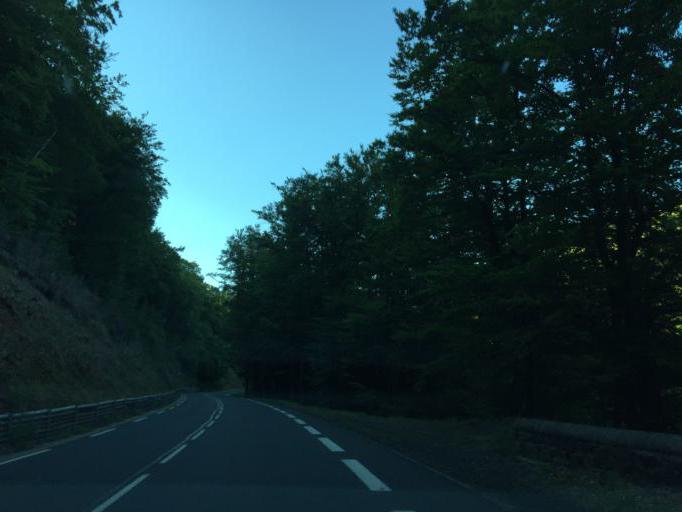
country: FR
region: Auvergne
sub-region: Departement de la Haute-Loire
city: Bains
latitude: 44.9832
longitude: 3.6732
